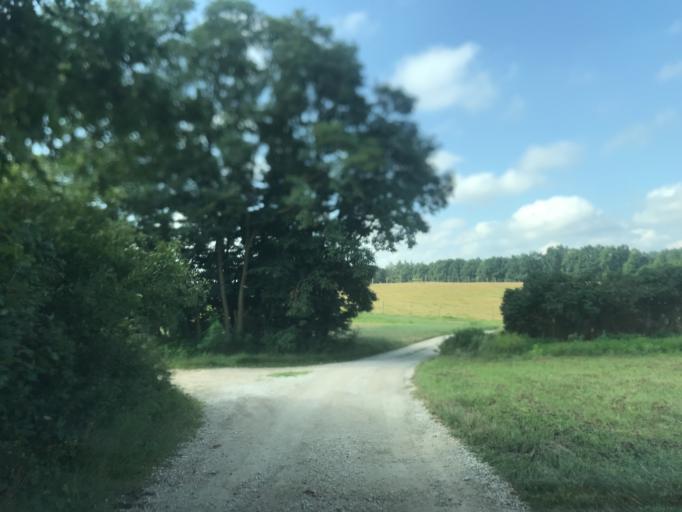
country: PL
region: Kujawsko-Pomorskie
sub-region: Powiat brodnicki
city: Brodnica
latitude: 53.3456
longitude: 19.4684
